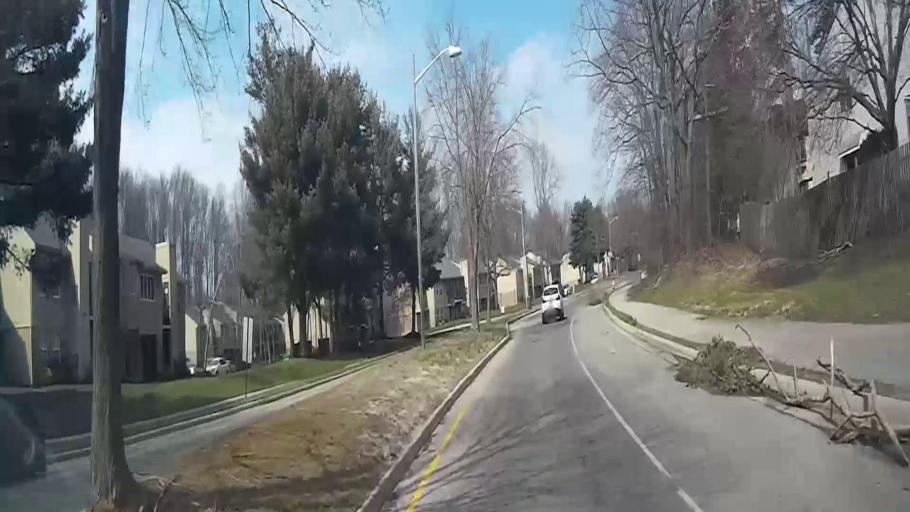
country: US
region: New Jersey
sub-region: Burlington County
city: Marlton
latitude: 39.8749
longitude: -74.8659
